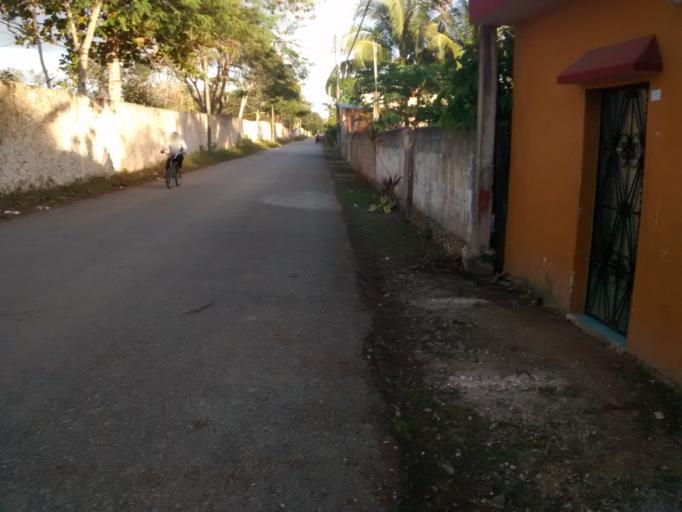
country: MX
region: Yucatan
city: Valladolid
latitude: 20.6827
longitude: -88.1861
